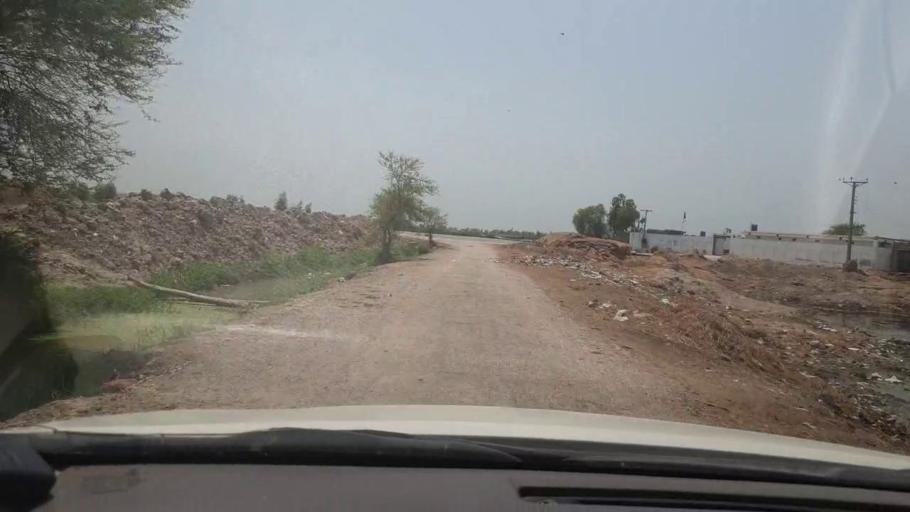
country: PK
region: Sindh
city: Garhi Yasin
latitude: 27.9080
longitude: 68.5536
